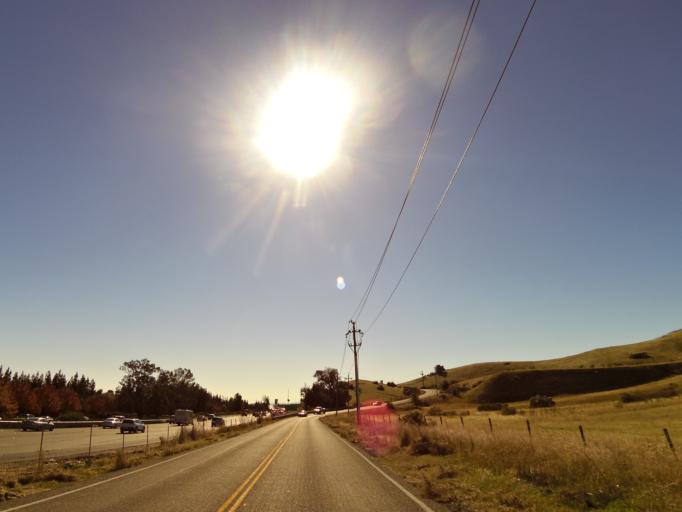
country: US
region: California
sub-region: Solano County
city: Fairfield
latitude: 38.3051
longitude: -122.0343
